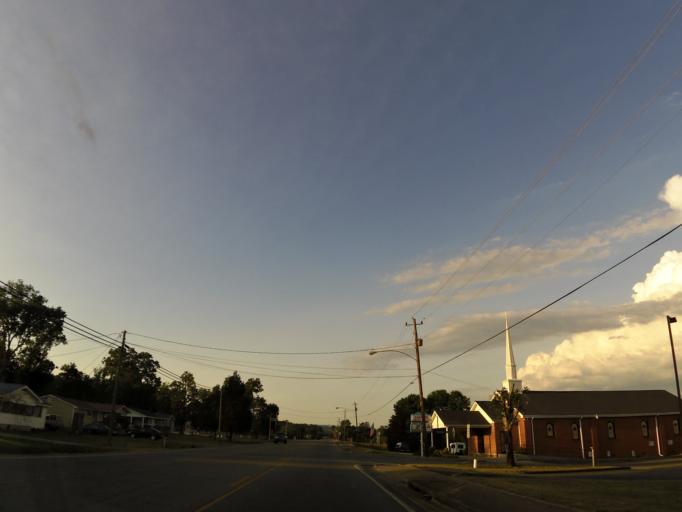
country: US
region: Georgia
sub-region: Dade County
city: Trenton
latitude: 34.8806
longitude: -85.5044
